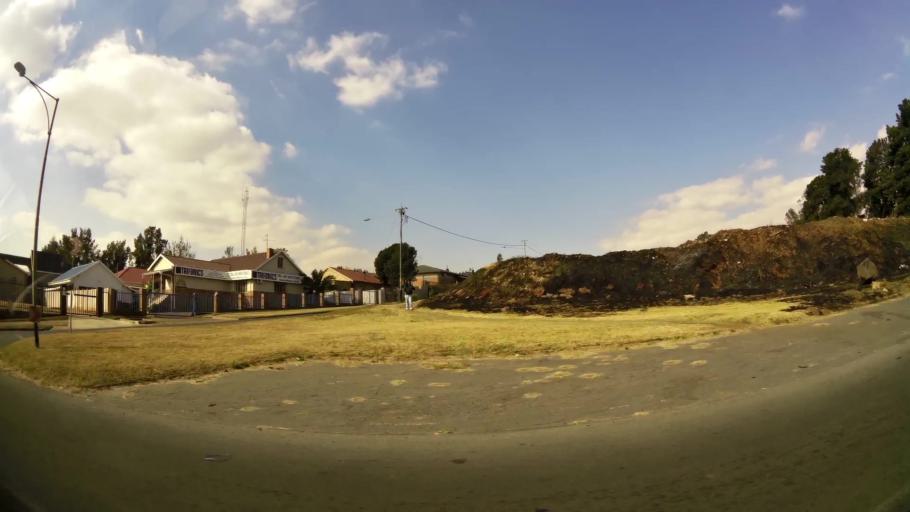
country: ZA
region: Gauteng
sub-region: West Rand District Municipality
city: Krugersdorp
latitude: -26.1044
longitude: 27.7660
